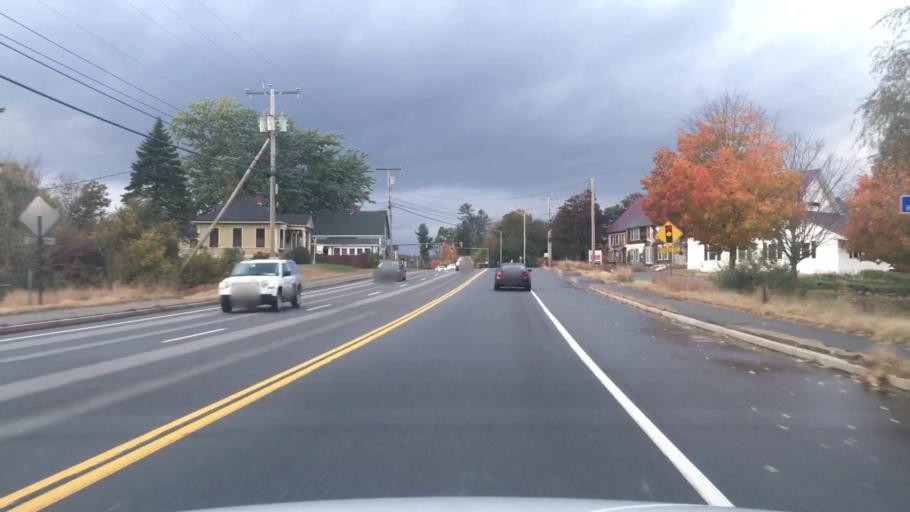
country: US
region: New Hampshire
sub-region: Merrimack County
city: Epsom
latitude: 43.2259
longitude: -71.3484
